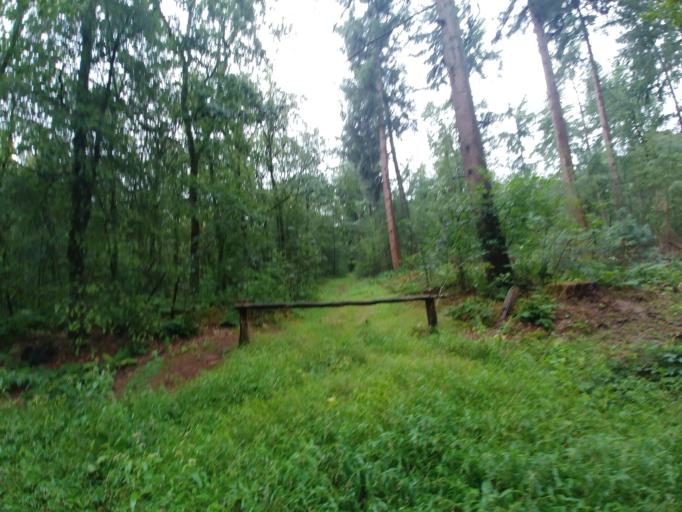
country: NL
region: Utrecht
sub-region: Gemeente Utrechtse Heuvelrug
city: Overberg
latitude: 52.0359
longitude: 5.4765
